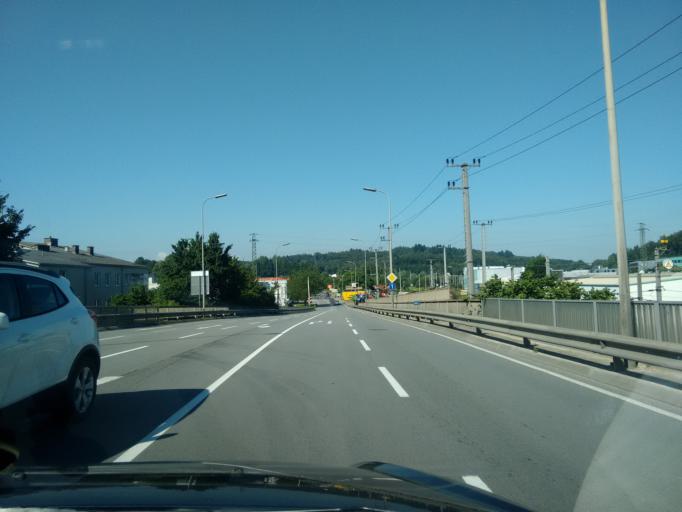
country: AT
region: Upper Austria
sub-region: Politischer Bezirk Vocklabruck
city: Attnang-Puchheim
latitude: 48.0077
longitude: 13.7156
